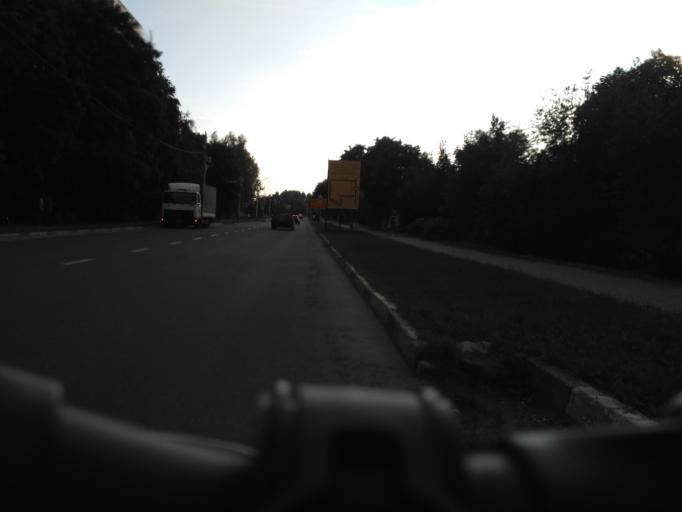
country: RU
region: Moskovskaya
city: Dubna
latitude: 56.7452
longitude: 37.1757
